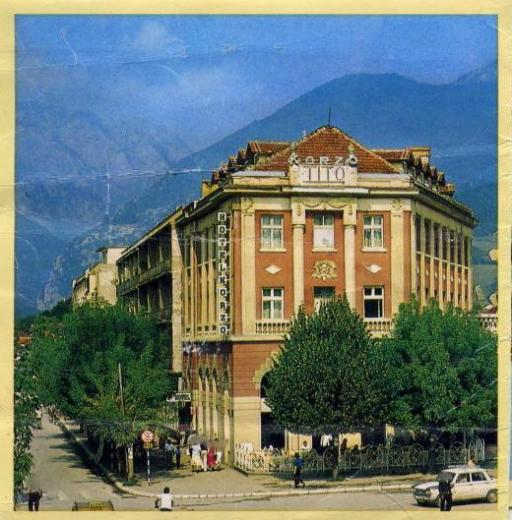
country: XK
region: Pec
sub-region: Komuna e Pejes
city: Peje
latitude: 42.6592
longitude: 20.2886
